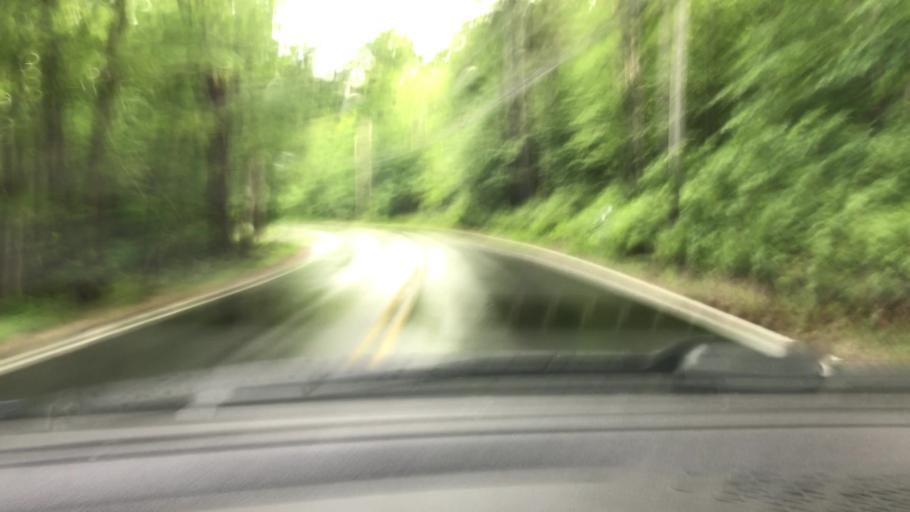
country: US
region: New Hampshire
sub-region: Merrimack County
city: Epsom
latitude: 43.2017
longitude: -71.2738
